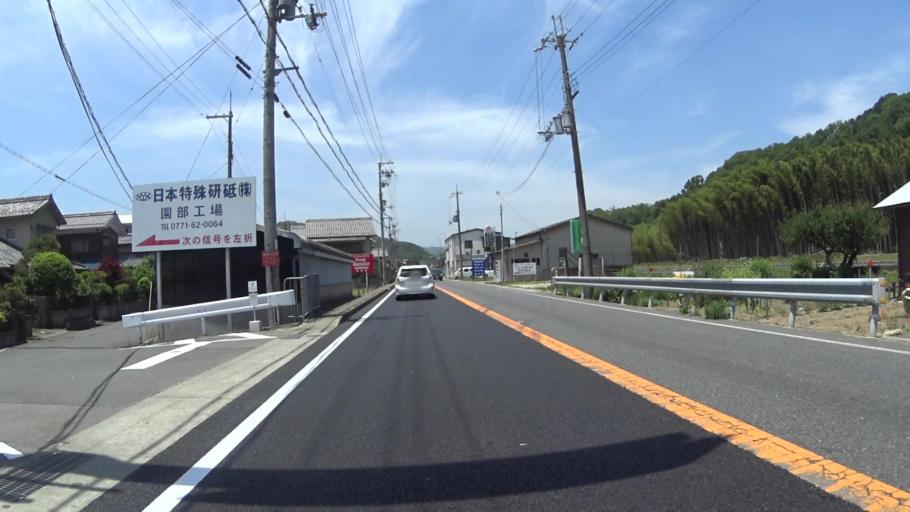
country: JP
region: Kyoto
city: Kameoka
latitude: 35.1007
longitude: 135.4899
